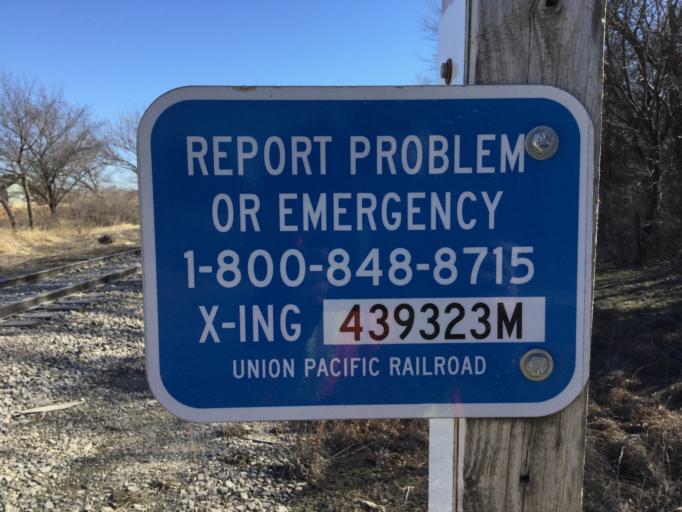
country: US
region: Kansas
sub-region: Butler County
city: Towanda
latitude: 37.7940
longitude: -97.0621
